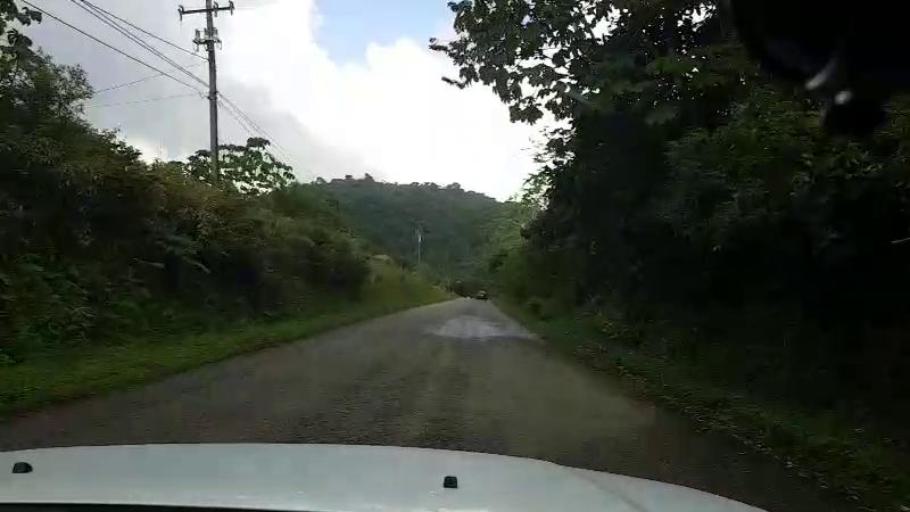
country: BZ
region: Stann Creek
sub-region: Dangriga
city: Dangriga
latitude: 17.0031
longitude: -88.4395
